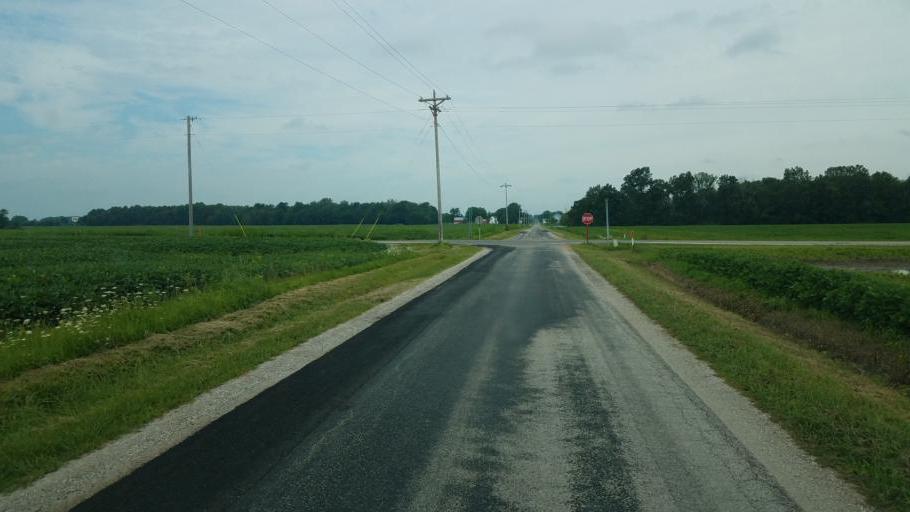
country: US
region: Ohio
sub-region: Morrow County
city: Cardington
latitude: 40.4998
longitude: -82.9622
